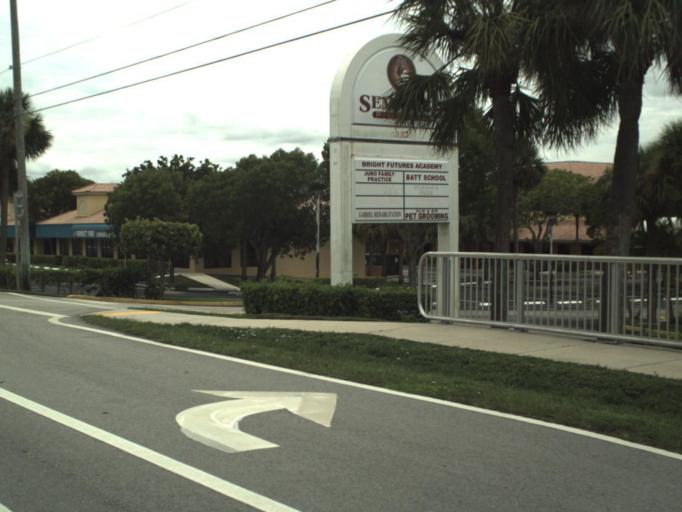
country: US
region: Florida
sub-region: Palm Beach County
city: Juno Beach
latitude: 26.8703
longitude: -80.0552
